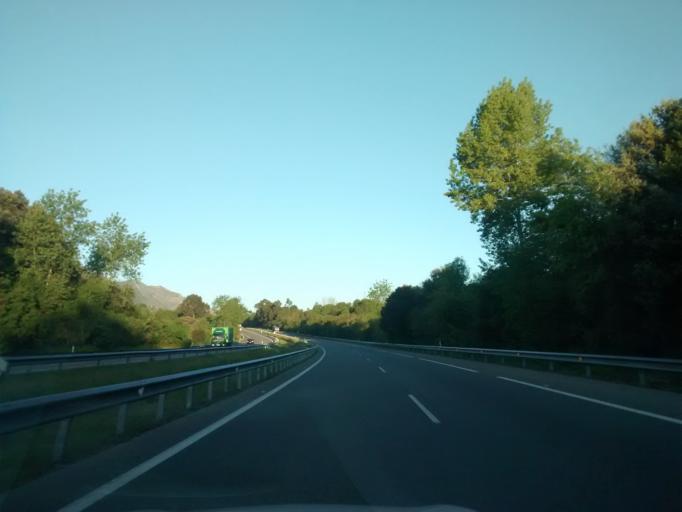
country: ES
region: Asturias
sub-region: Province of Asturias
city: Ribadesella
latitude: 43.4455
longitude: -4.9200
